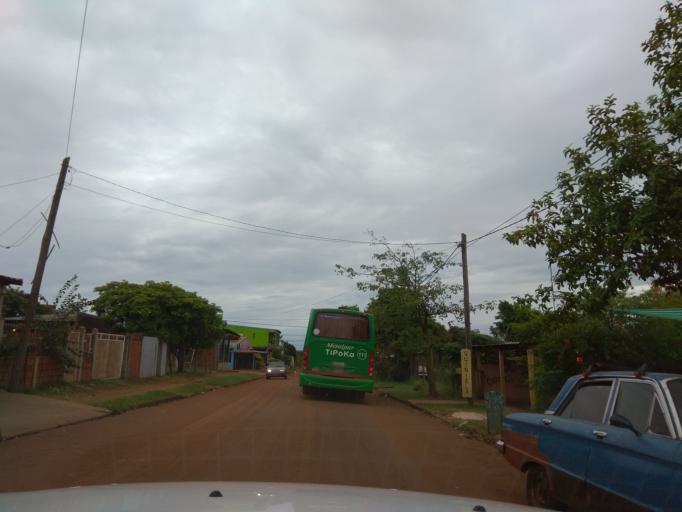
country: AR
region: Misiones
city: Garupa
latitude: -27.4397
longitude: -55.8602
